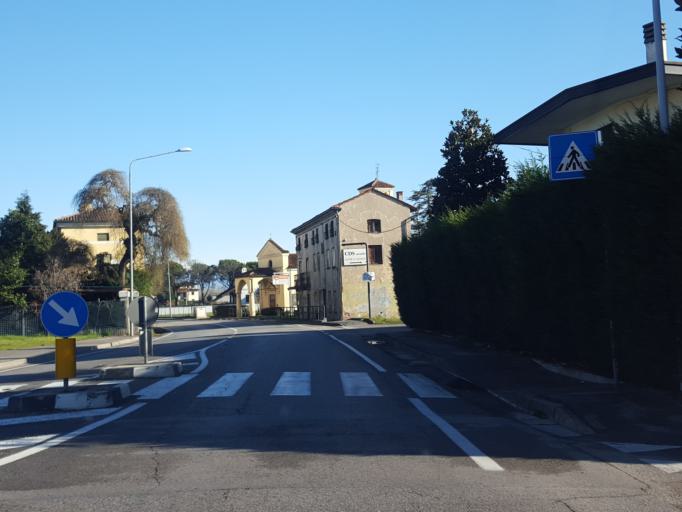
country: IT
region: Veneto
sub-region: Provincia di Vicenza
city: Vicenza
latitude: 45.5731
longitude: 11.5497
